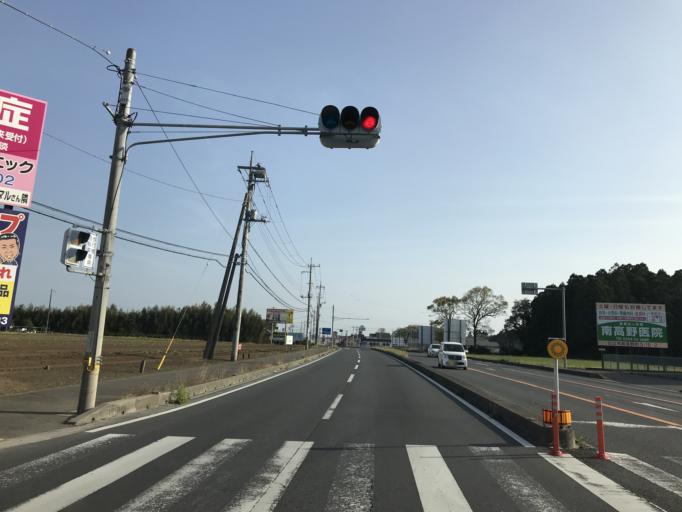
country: JP
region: Ibaraki
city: Hitachi-Naka
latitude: 36.4042
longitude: 140.5809
